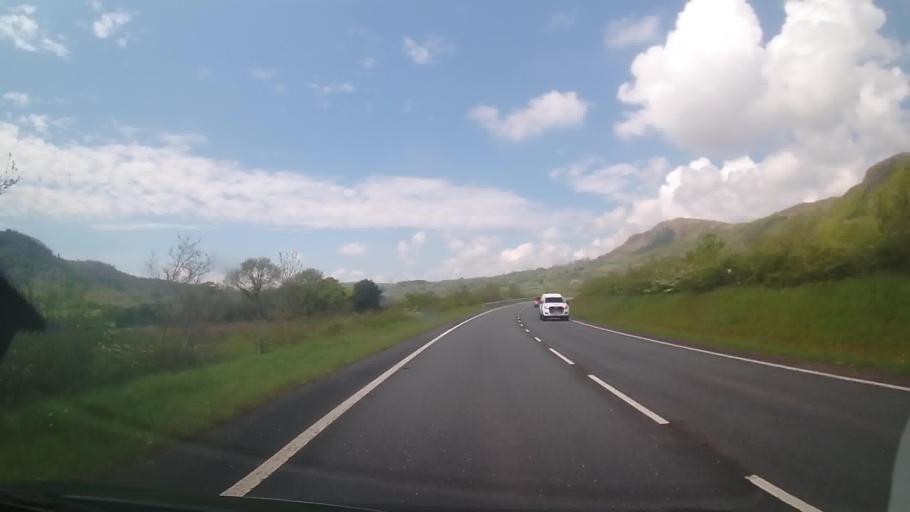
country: GB
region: Wales
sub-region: Gwynedd
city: Porthmadog
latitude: 52.9365
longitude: -4.1440
